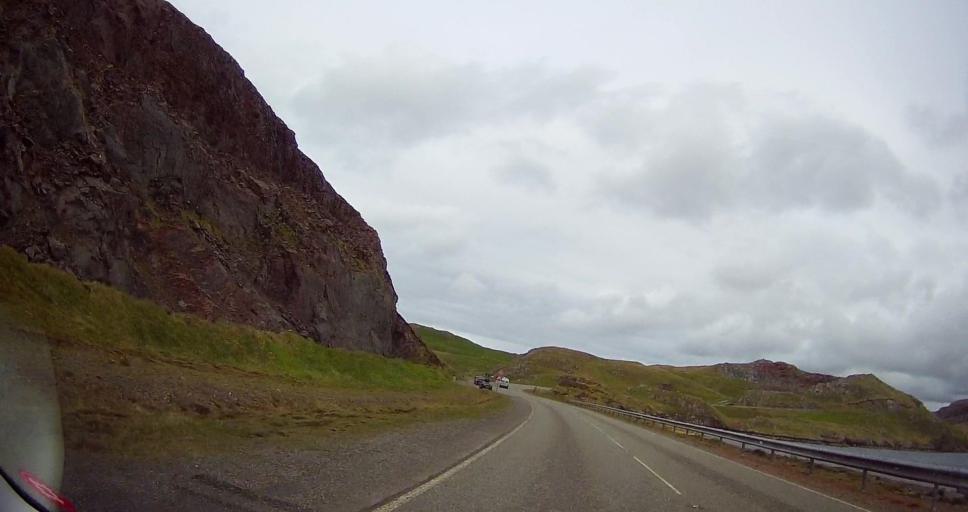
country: GB
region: Scotland
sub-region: Shetland Islands
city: Lerwick
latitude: 60.3964
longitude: -1.3812
